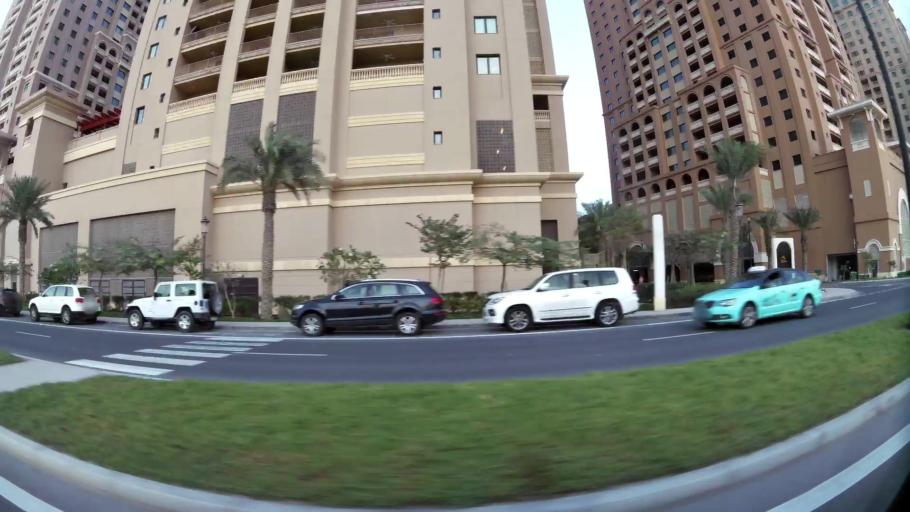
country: QA
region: Baladiyat ad Dawhah
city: Doha
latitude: 25.3680
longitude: 51.5380
